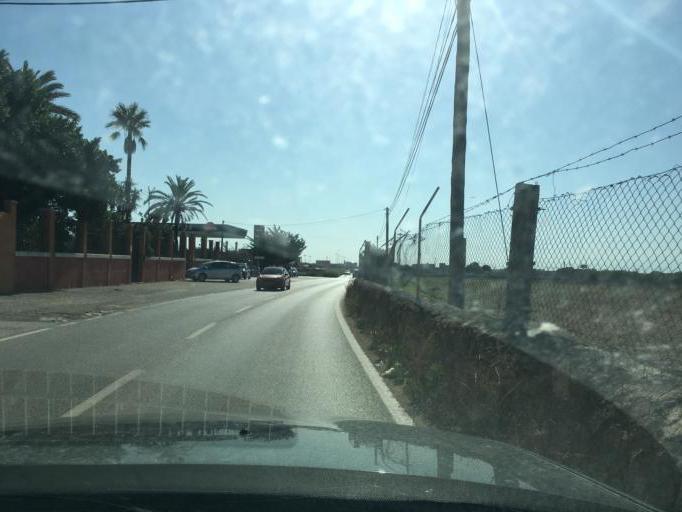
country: ES
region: Balearic Islands
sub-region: Illes Balears
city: Palma
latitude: 39.5769
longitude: 2.6850
